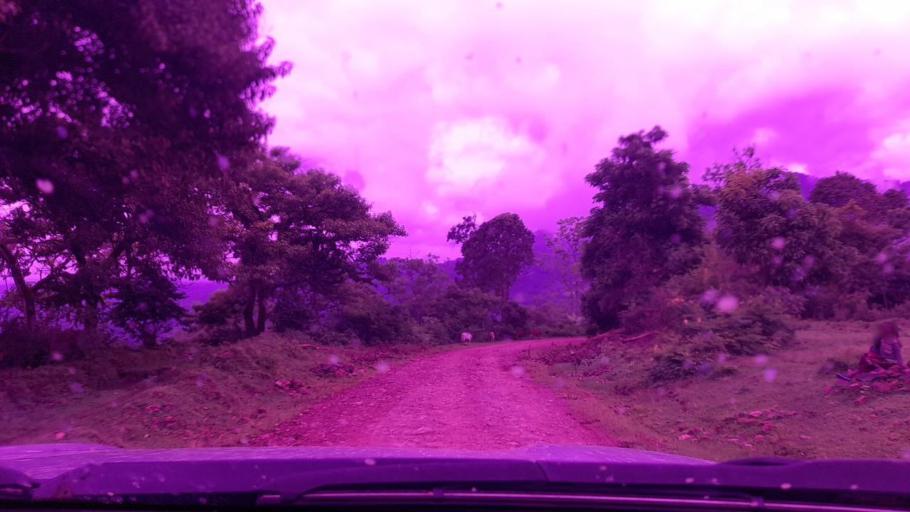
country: ET
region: Southern Nations, Nationalities, and People's Region
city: Bonga
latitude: 7.5479
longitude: 35.8438
